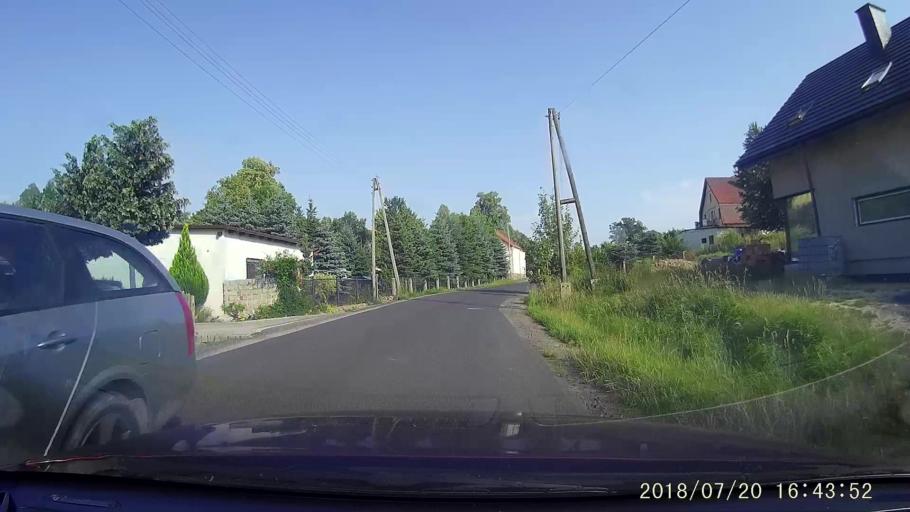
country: PL
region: Lower Silesian Voivodeship
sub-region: Powiat lubanski
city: Siekierczyn
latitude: 51.0708
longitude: 15.1631
